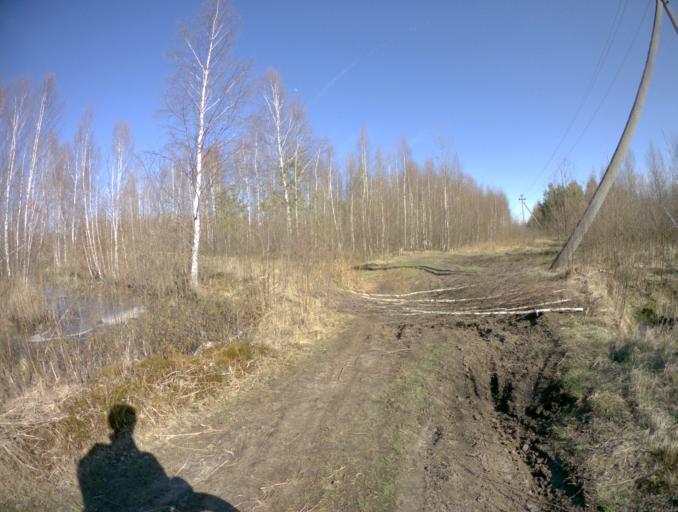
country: RU
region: Vladimir
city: Ivanishchi
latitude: 55.7363
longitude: 40.4089
